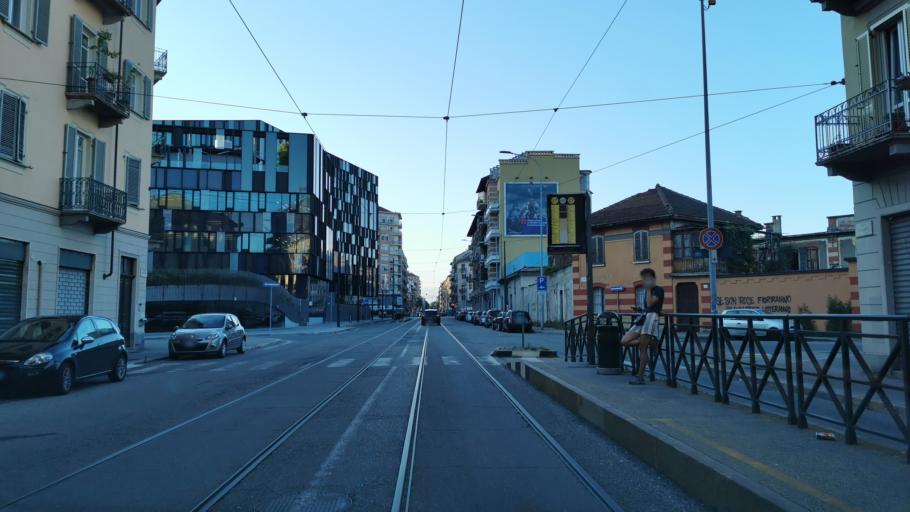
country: IT
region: Piedmont
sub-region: Provincia di Torino
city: Turin
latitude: 45.0795
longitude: 7.6926
